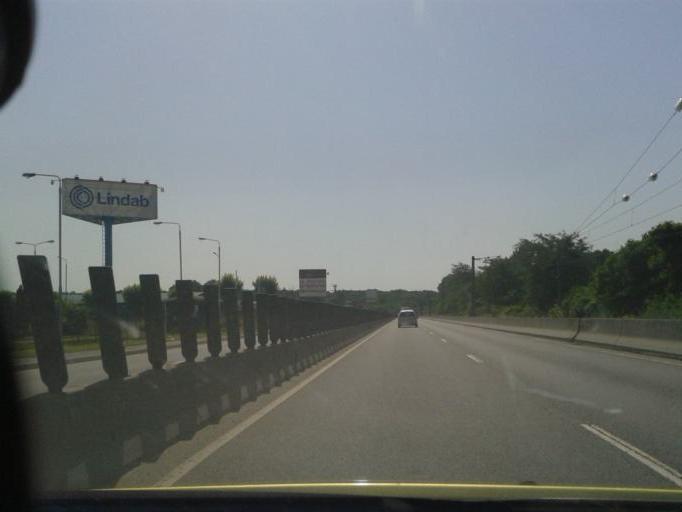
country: RO
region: Ilfov
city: Stefanestii de Jos
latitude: 44.5193
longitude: 26.1780
